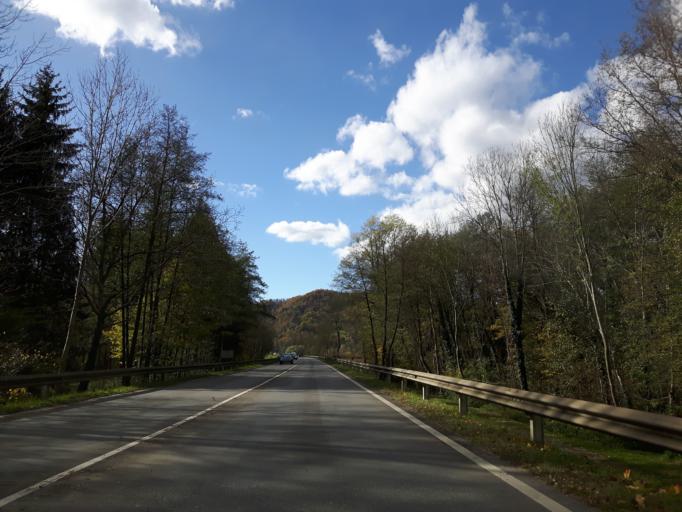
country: AT
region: Styria
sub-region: Politischer Bezirk Leibnitz
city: Kaindorf an der Sulm
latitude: 46.7974
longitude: 15.5369
